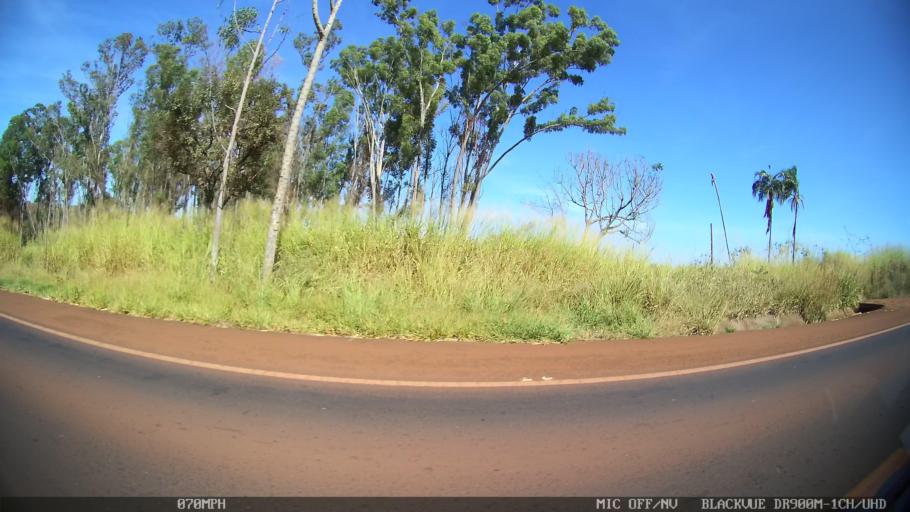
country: BR
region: Sao Paulo
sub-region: Sao Joaquim Da Barra
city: Sao Joaquim da Barra
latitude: -20.5466
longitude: -47.7710
